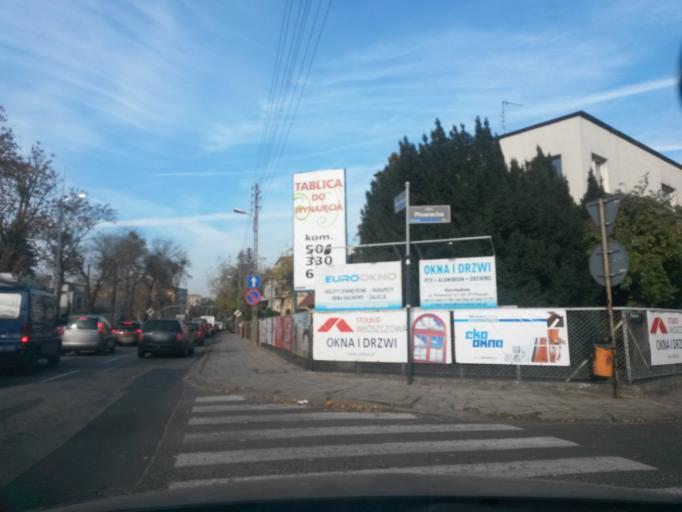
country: PL
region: Greater Poland Voivodeship
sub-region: Poznan
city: Poznan
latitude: 52.3979
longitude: 16.8783
